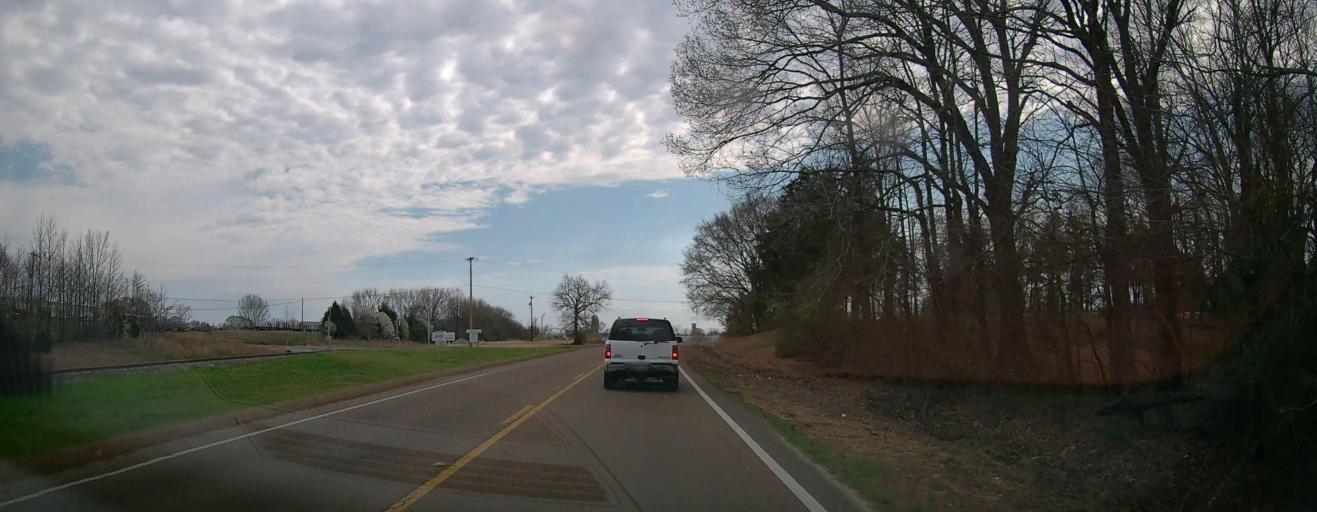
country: US
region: Mississippi
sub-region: Marshall County
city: Byhalia
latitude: 34.8689
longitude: -89.6704
